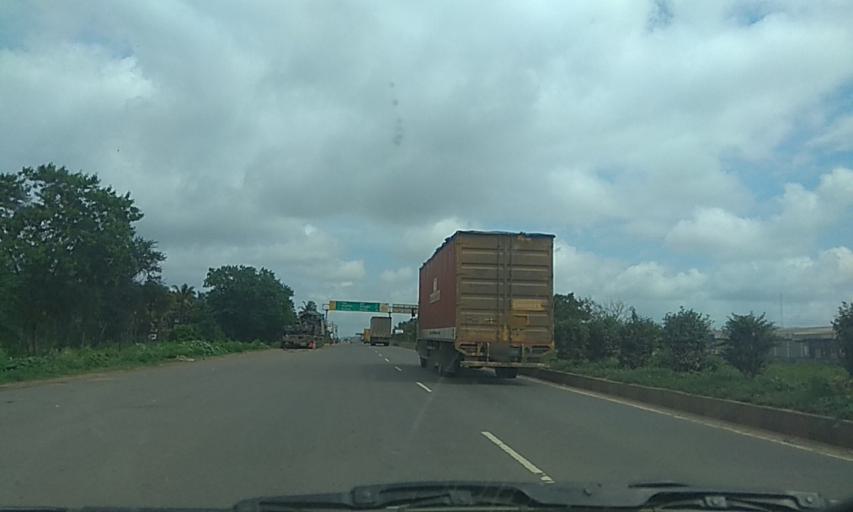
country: IN
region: Karnataka
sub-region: Dharwad
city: Hubli
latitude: 15.3119
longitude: 75.1449
